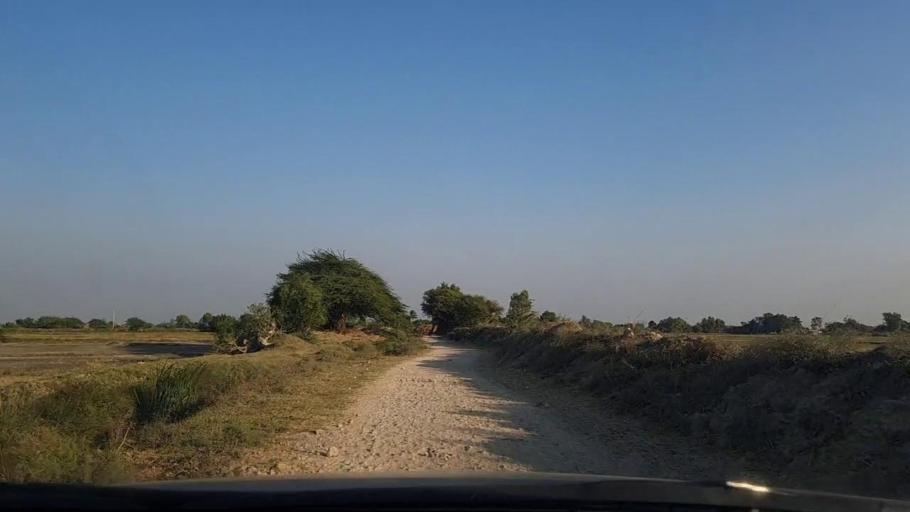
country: PK
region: Sindh
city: Mirpur Sakro
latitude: 24.5232
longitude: 67.6500
